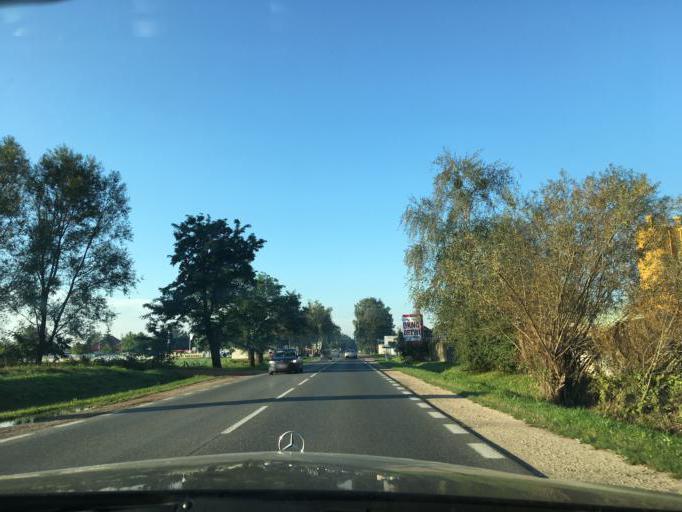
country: PL
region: Masovian Voivodeship
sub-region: Powiat pruszkowski
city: Otrebusy
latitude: 52.1413
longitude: 20.7718
